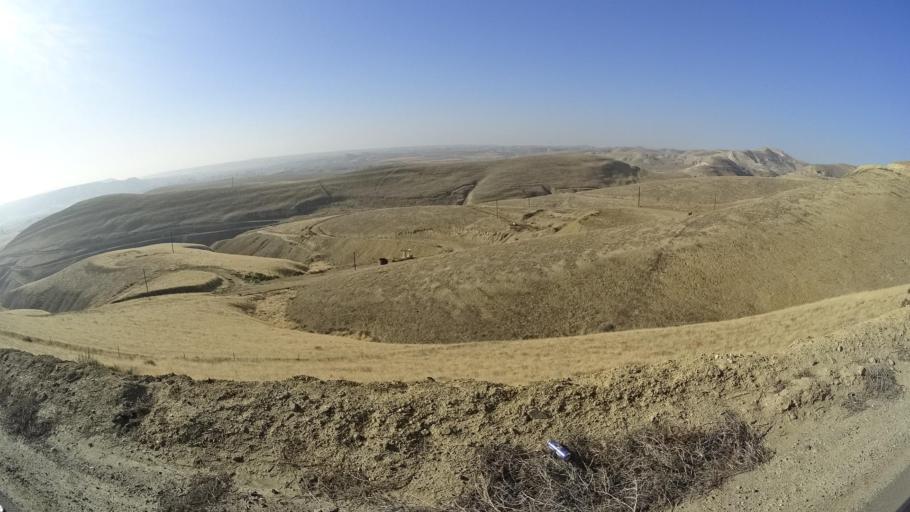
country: US
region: California
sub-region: Kern County
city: Oildale
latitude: 35.4566
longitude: -118.8728
